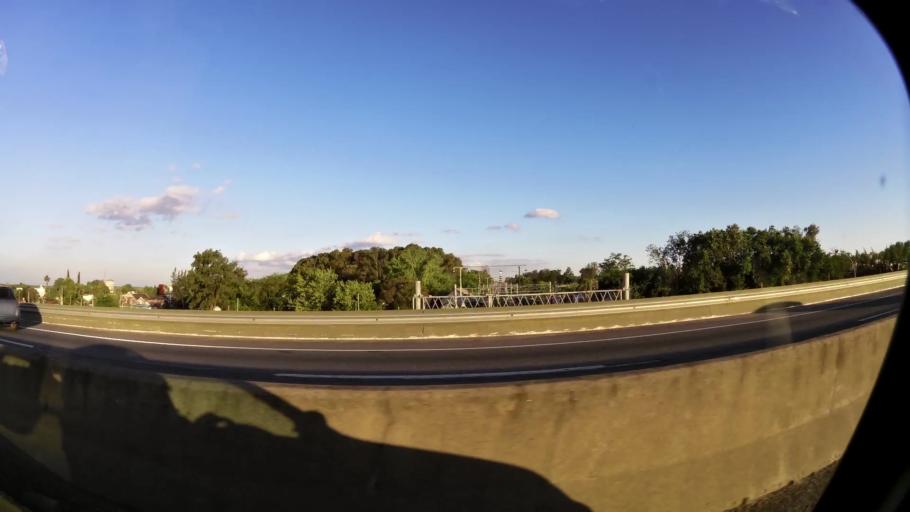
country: AR
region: Buenos Aires
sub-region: Partido de Quilmes
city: Quilmes
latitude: -34.7904
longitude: -58.1570
